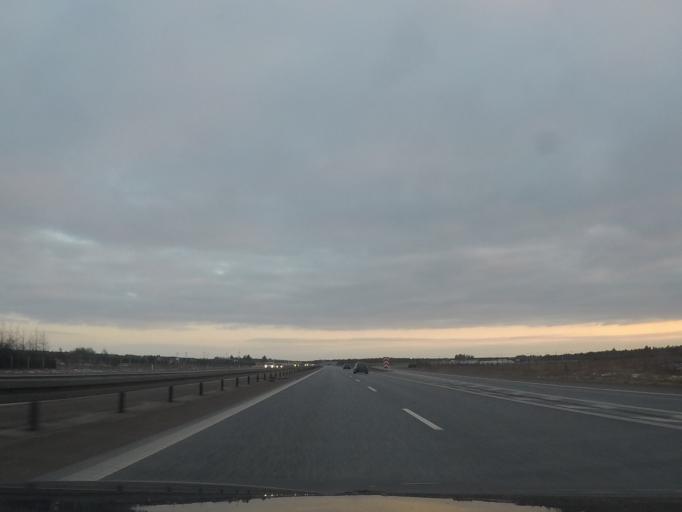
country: DK
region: Central Jutland
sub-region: Herning Kommune
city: Lind
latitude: 56.0433
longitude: 9.0018
